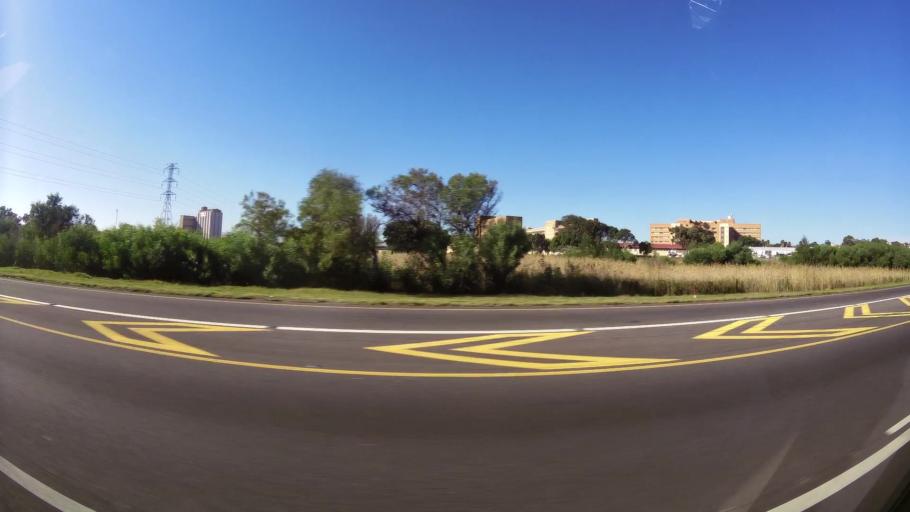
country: ZA
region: Eastern Cape
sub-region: Nelson Mandela Bay Metropolitan Municipality
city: Port Elizabeth
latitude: -33.9219
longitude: 25.5689
